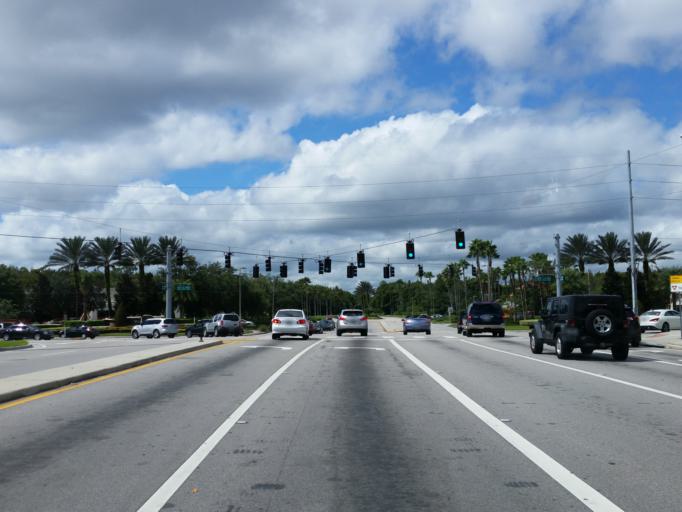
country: US
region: Florida
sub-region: Hillsborough County
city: Pebble Creek
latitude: 28.1436
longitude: -82.3527
